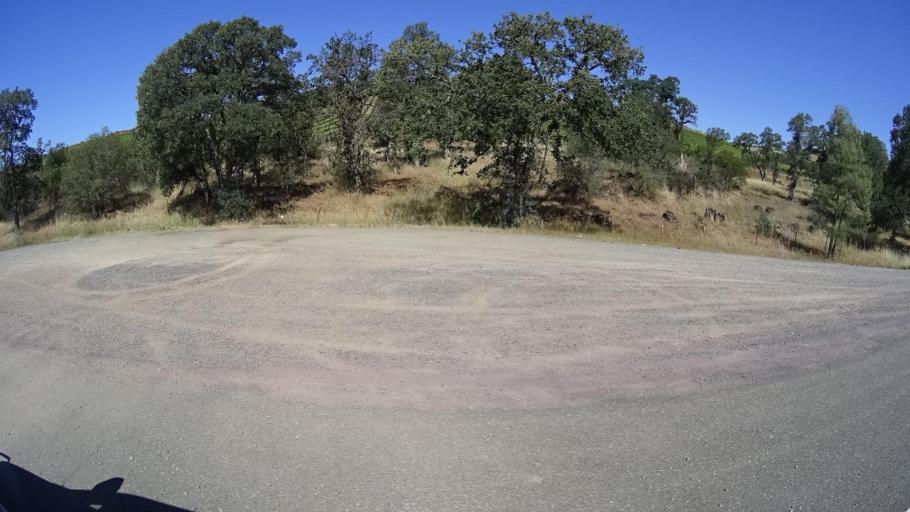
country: US
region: California
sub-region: Lake County
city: Clearlake
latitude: 38.9983
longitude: -122.6062
